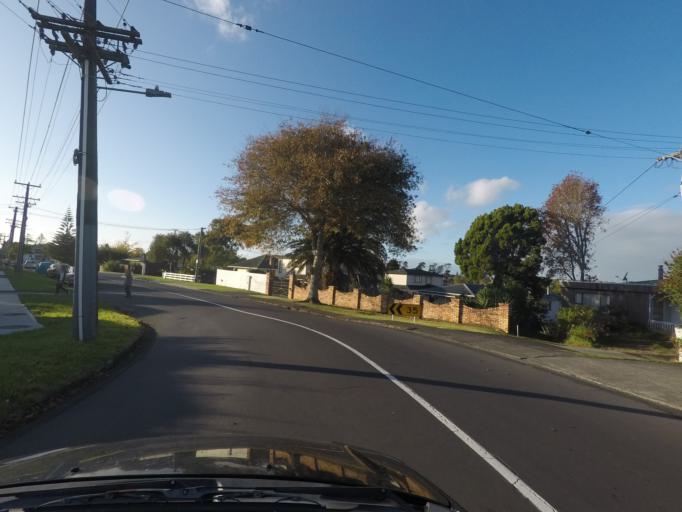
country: NZ
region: Auckland
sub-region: Auckland
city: Waitakere
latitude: -36.9043
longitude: 174.6766
